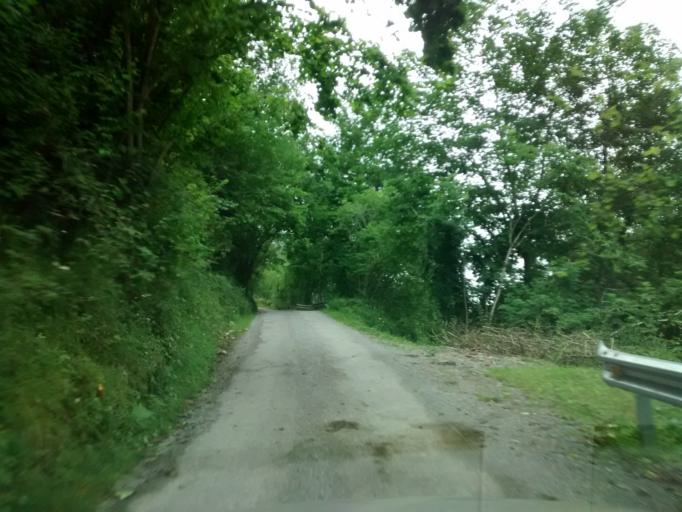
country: ES
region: Asturias
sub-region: Province of Asturias
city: Pilona
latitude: 43.2772
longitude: -5.3501
